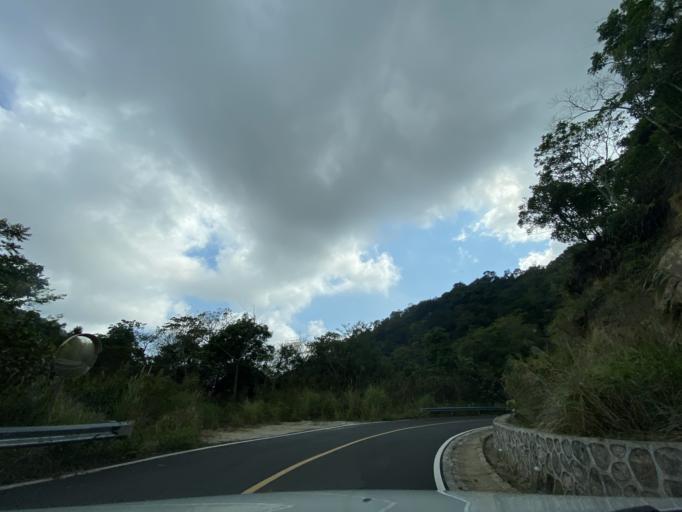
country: CN
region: Hainan
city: Diaoluoshan
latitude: 18.7052
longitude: 109.8826
